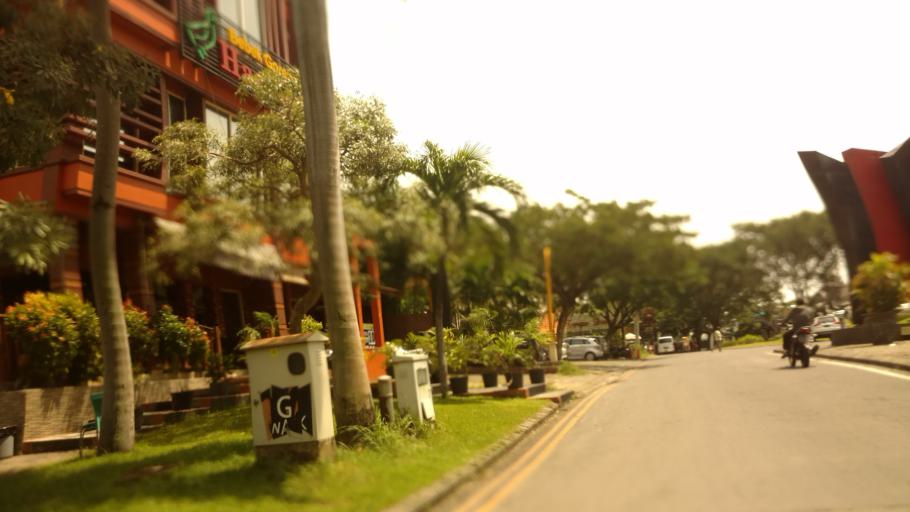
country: ID
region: East Java
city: Driyorejo
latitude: -7.2918
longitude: 112.6546
